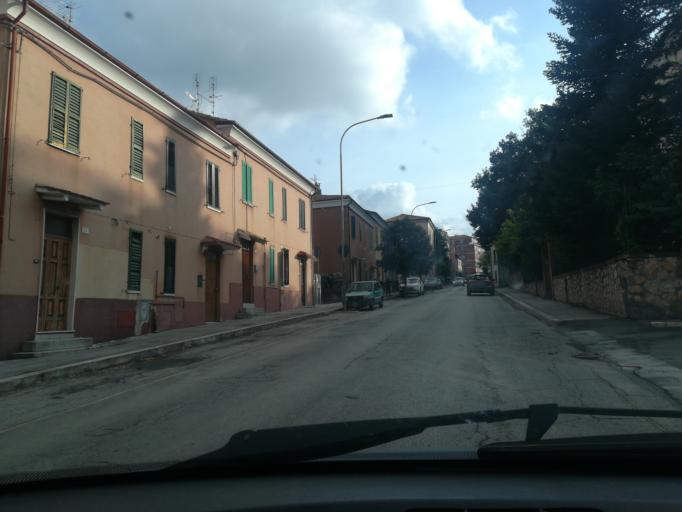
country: IT
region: The Marches
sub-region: Provincia di Macerata
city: Macerata
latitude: 43.3041
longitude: 13.4611
